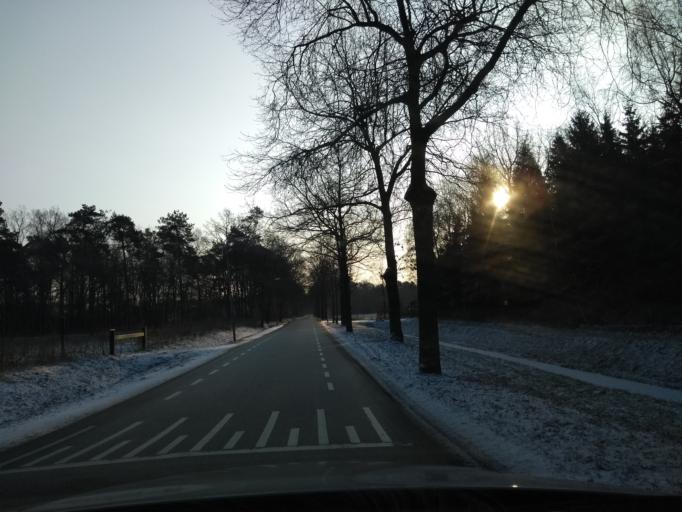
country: NL
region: Overijssel
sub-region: Gemeente Hof van Twente
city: Delden
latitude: 52.2178
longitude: 6.7287
